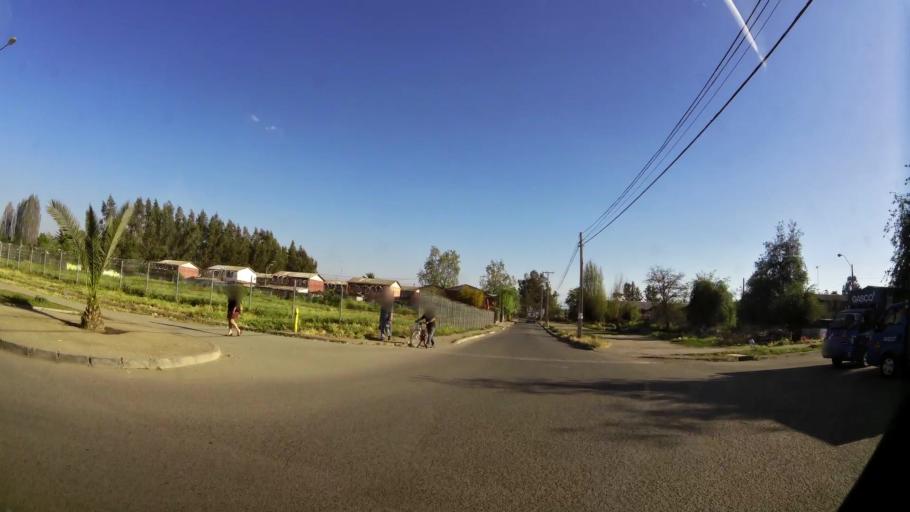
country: CL
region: Santiago Metropolitan
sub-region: Provincia de Talagante
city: Penaflor
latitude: -33.6040
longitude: -70.8664
